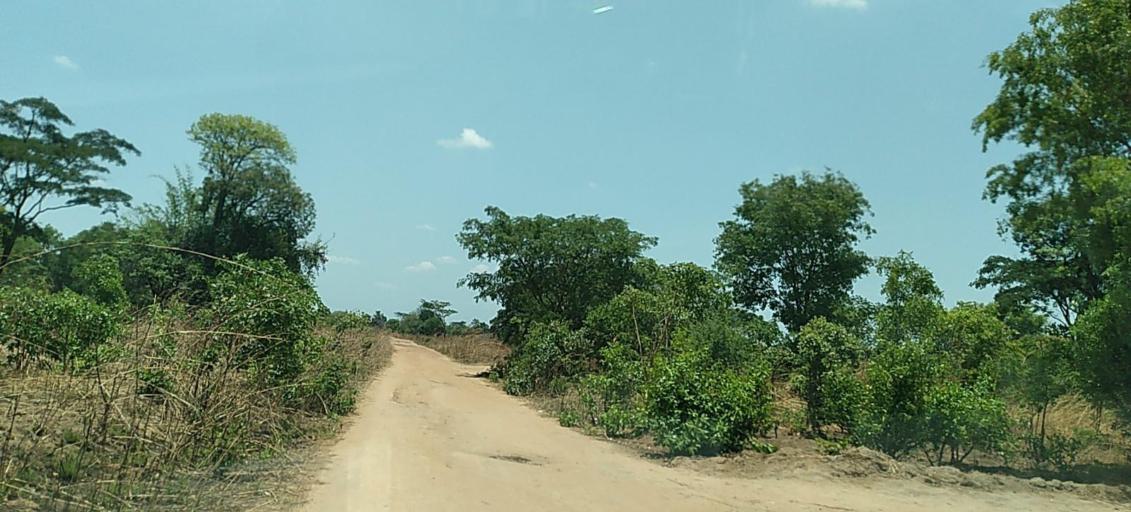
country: ZM
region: Copperbelt
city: Luanshya
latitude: -13.0825
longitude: 28.4055
